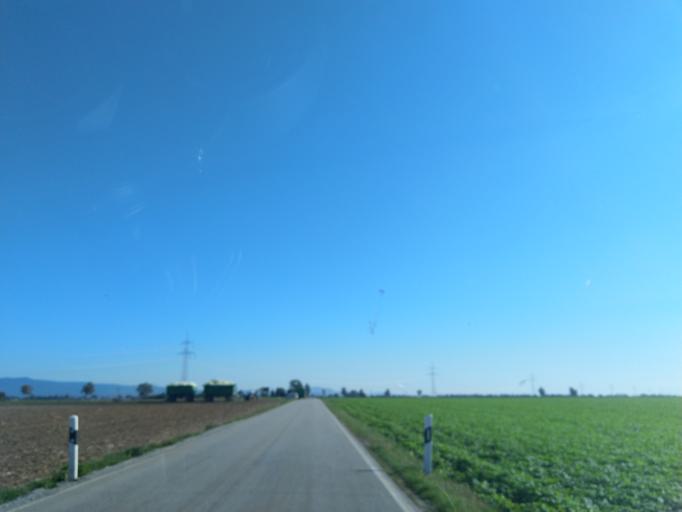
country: DE
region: Bavaria
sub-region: Lower Bavaria
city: Stephansposching
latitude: 48.7931
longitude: 12.7711
